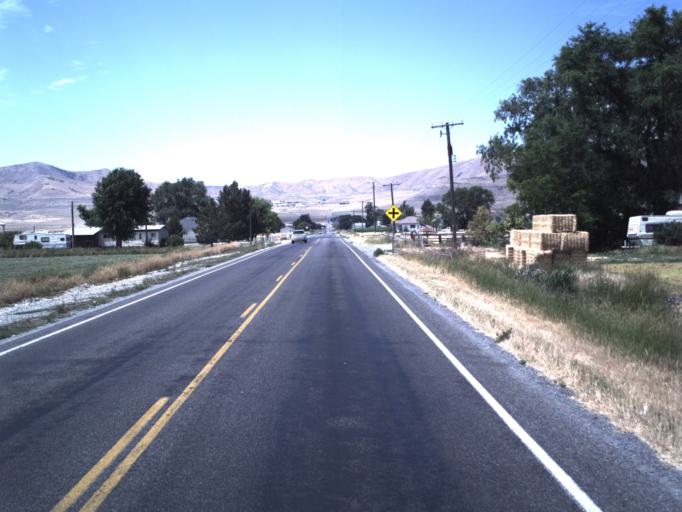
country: US
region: Utah
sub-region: Box Elder County
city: Tremonton
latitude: 41.7097
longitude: -112.2566
